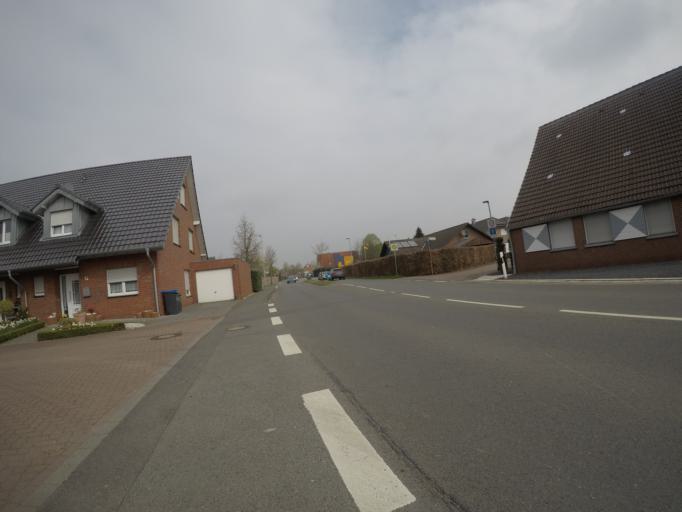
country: DE
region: North Rhine-Westphalia
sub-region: Regierungsbezirk Munster
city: Isselburg
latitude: 51.8581
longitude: 6.5027
